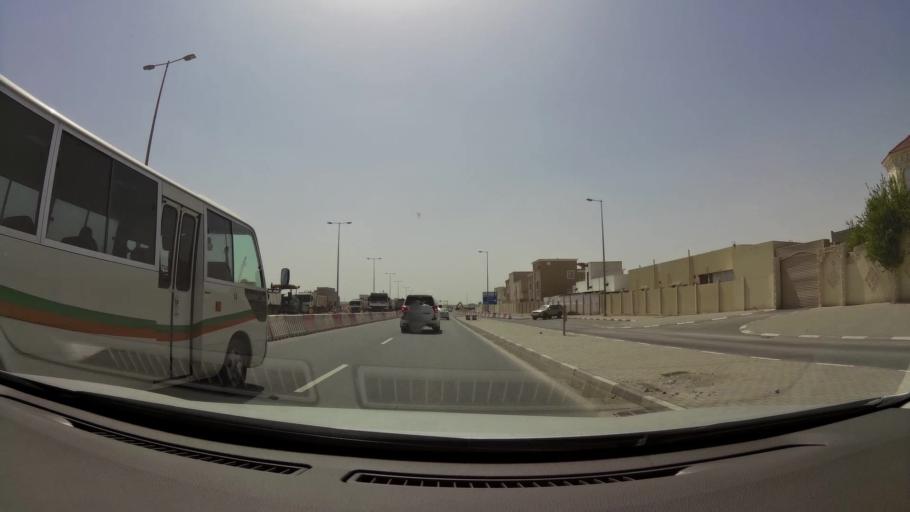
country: QA
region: Baladiyat Umm Salal
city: Umm Salal Muhammad
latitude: 25.3747
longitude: 51.4650
